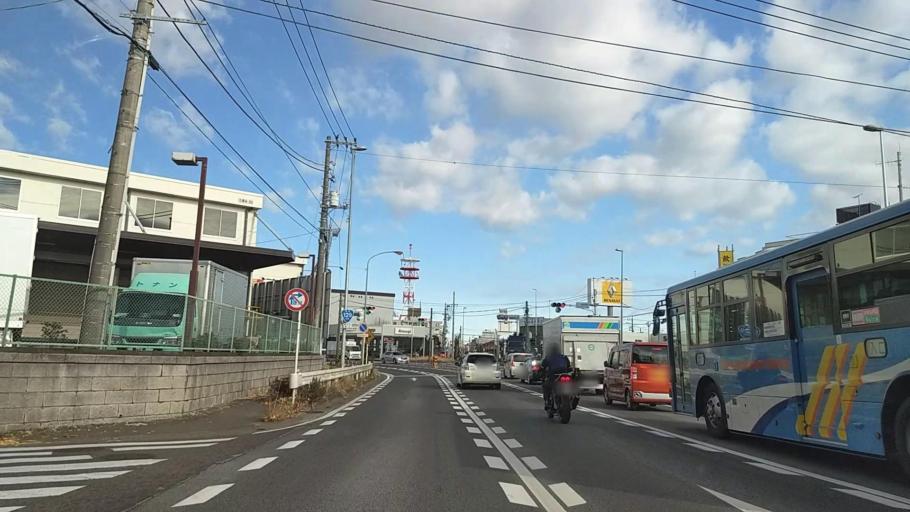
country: JP
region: Kanagawa
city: Atsugi
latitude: 35.4137
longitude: 139.3628
